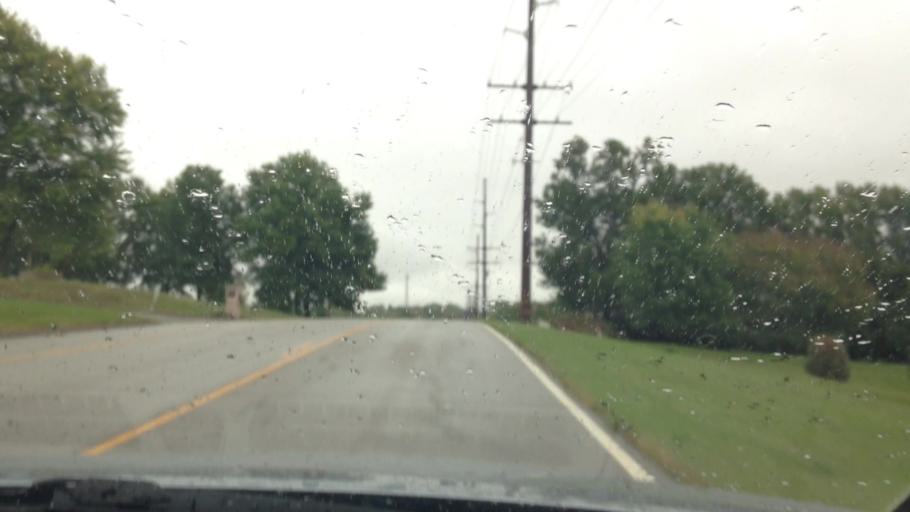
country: US
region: Missouri
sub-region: Platte County
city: Platte City
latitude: 39.3394
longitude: -94.7662
